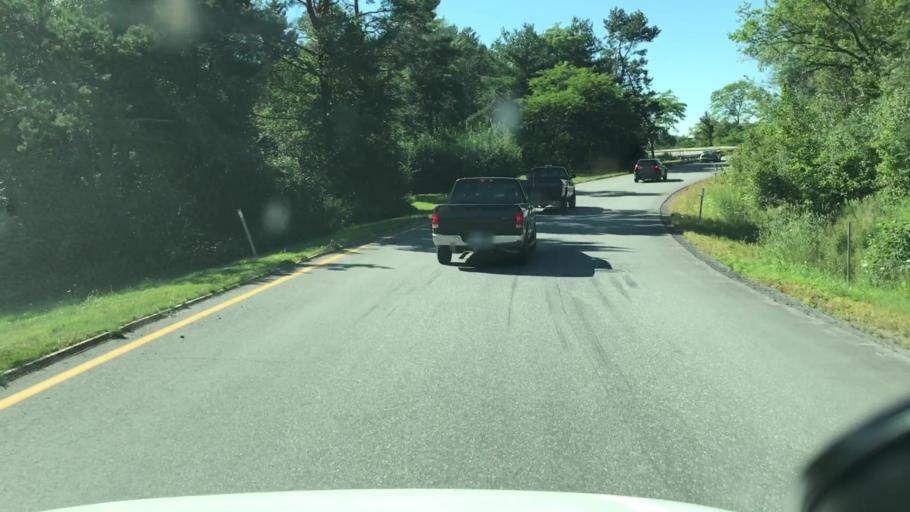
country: US
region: Maine
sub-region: Penobscot County
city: Bangor
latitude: 44.7870
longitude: -68.8045
